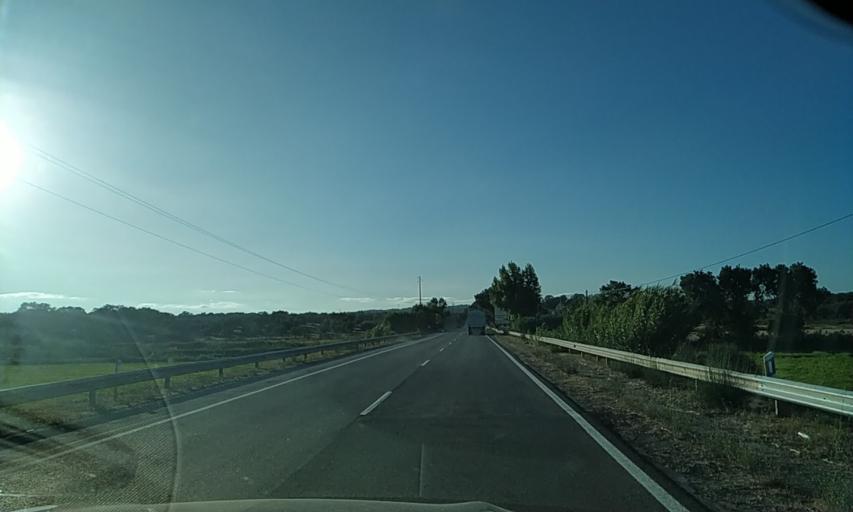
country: PT
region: Setubal
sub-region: Alcacer do Sal
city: Alcacer do Sal
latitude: 38.4715
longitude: -8.5877
